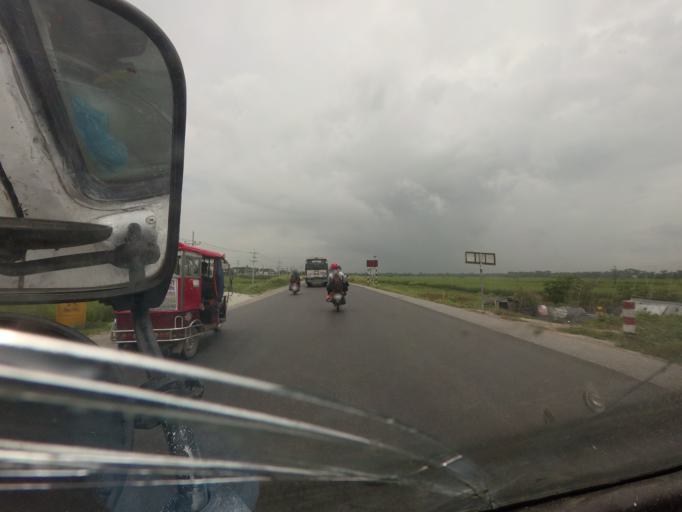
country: BD
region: Dhaka
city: Char Bhadrasan
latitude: 23.3705
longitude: 90.0374
